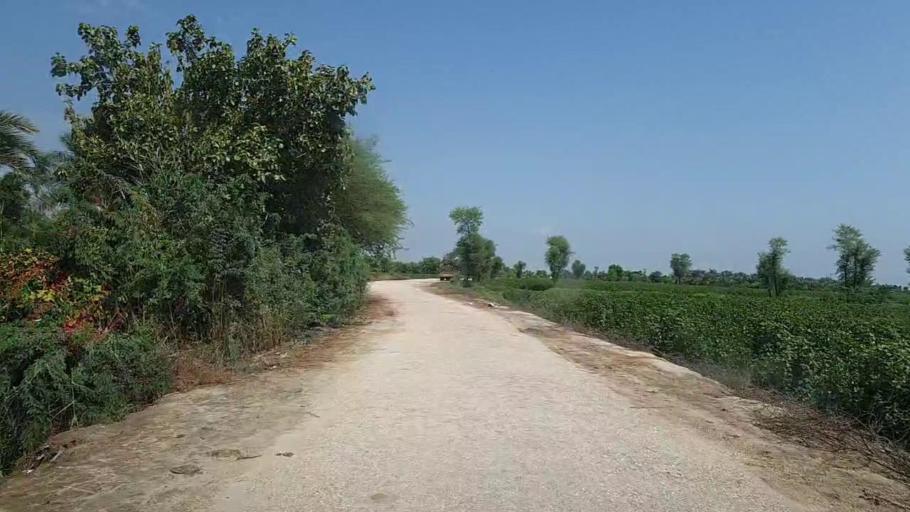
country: PK
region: Sindh
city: Bhiria
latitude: 26.8989
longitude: 68.2161
